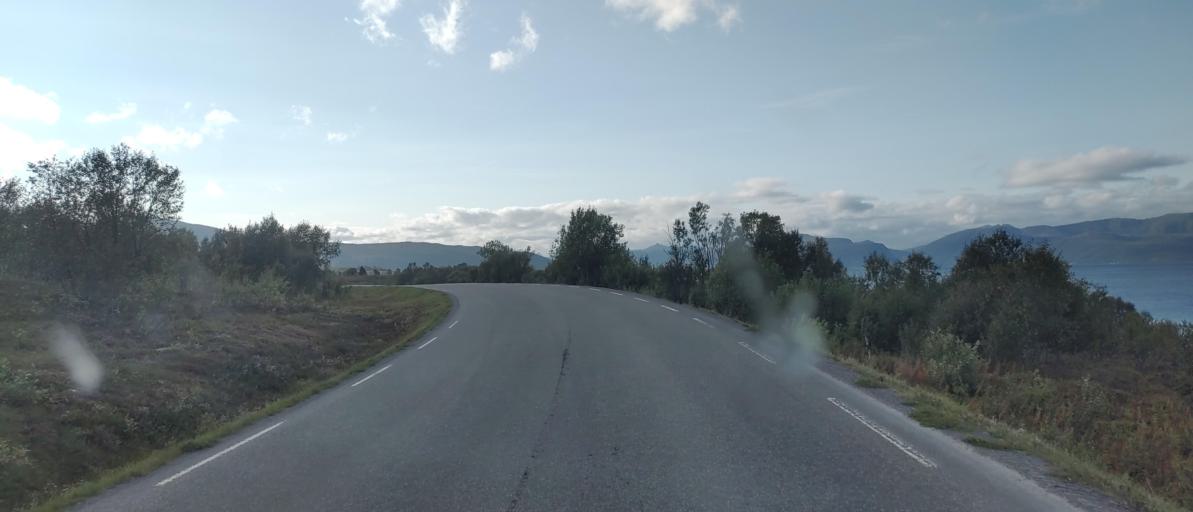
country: NO
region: Nordland
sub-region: Sortland
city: Sortland
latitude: 68.7228
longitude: 15.4930
